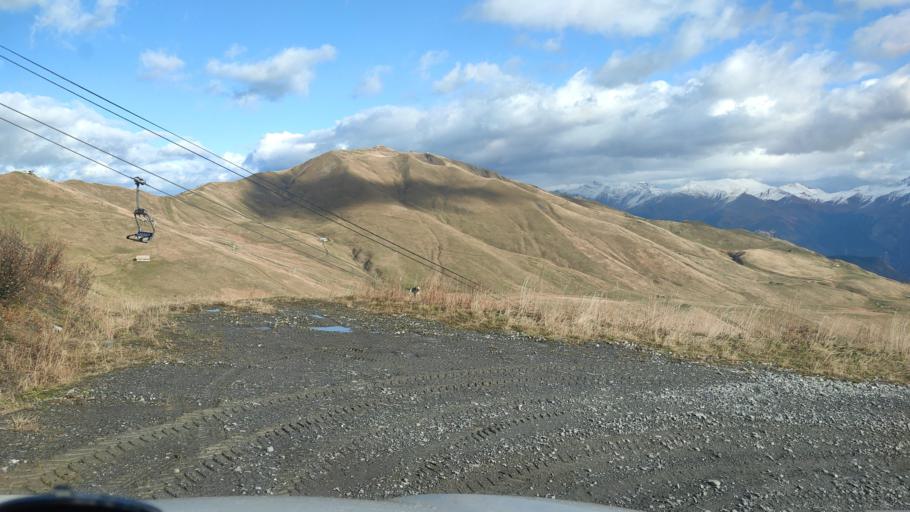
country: FR
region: Rhone-Alpes
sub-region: Departement de la Savoie
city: Saint-Etienne-de-Cuines
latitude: 45.2542
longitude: 6.2446
